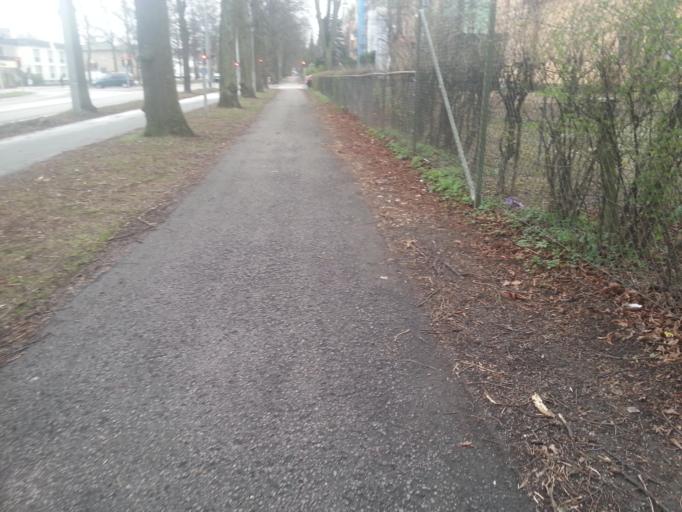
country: SE
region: OEstergoetland
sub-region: Norrkopings Kommun
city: Norrkoping
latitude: 58.5857
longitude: 16.1990
